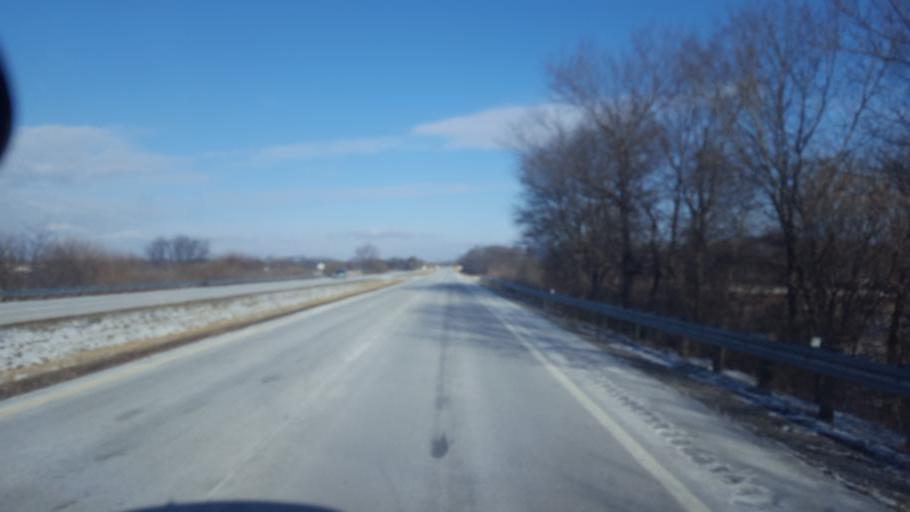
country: US
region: Ohio
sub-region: Pickaway County
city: Commercial Point
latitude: 39.8085
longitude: -82.9951
